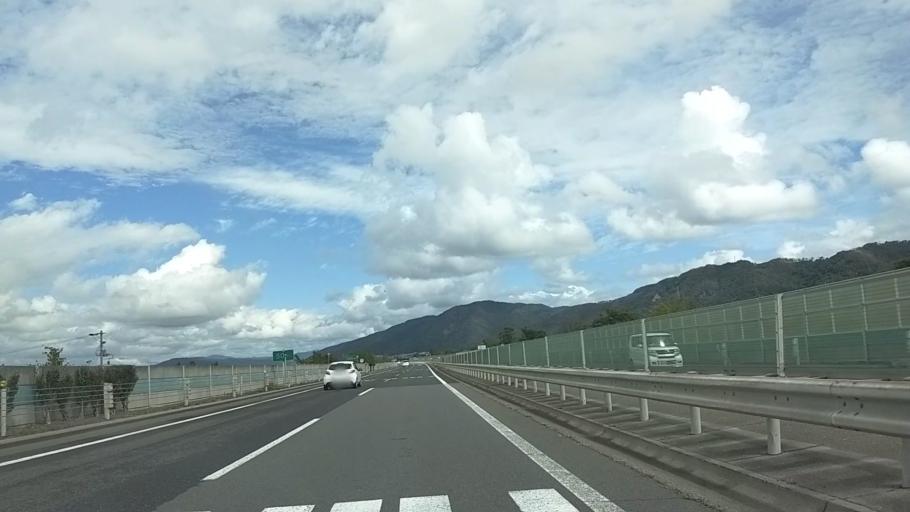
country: JP
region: Nagano
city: Toyoshina
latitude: 36.2743
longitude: 137.9308
